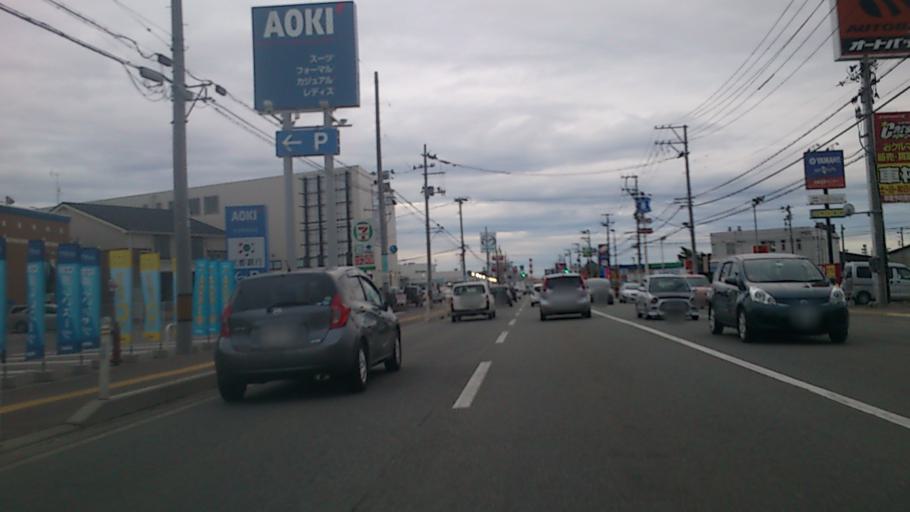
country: JP
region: Akita
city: Akita Shi
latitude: 39.7359
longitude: 140.0987
